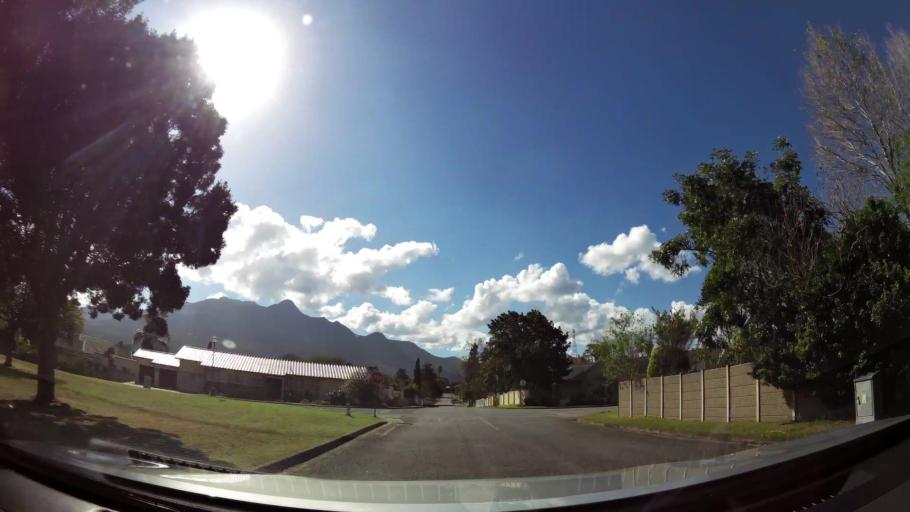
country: ZA
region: Western Cape
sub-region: Eden District Municipality
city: George
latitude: -33.9637
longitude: 22.4493
